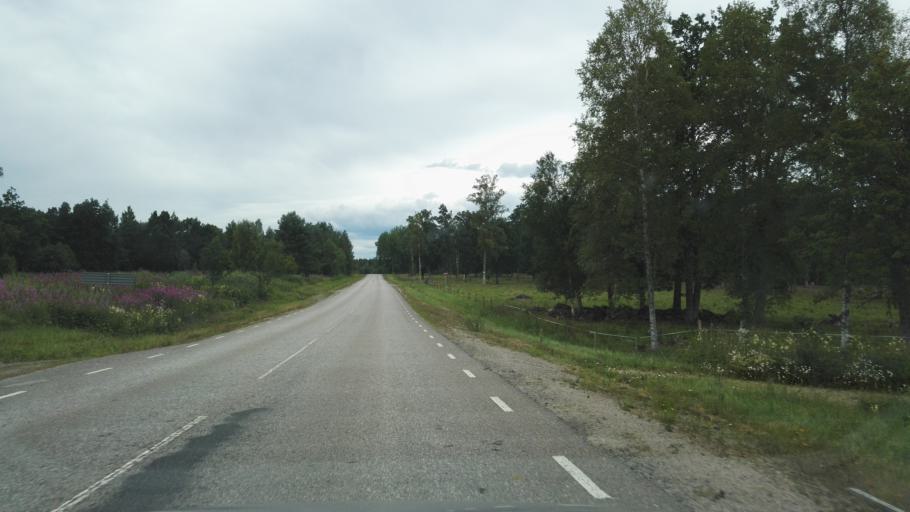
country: SE
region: Kronoberg
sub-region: Vaxjo Kommun
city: Braas
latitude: 57.1141
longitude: 14.9772
